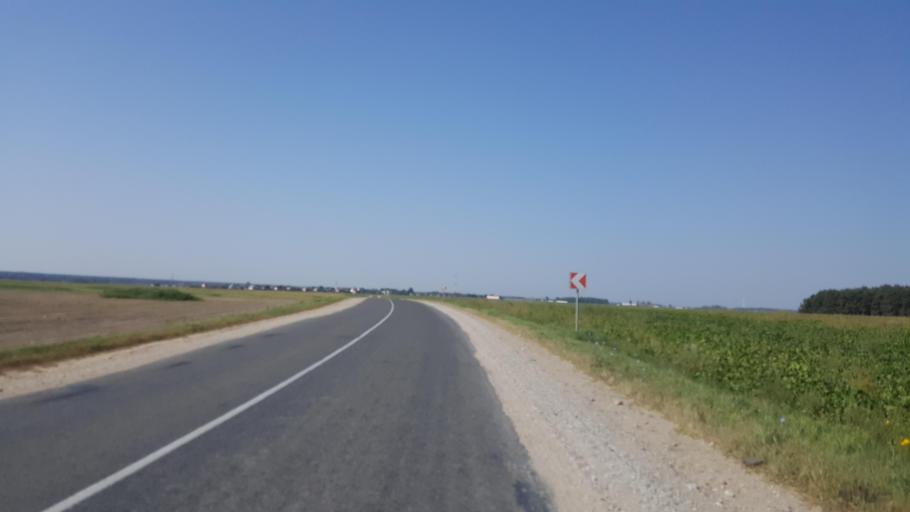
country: BY
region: Brest
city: Kamyanyets
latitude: 52.4175
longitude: 23.6554
